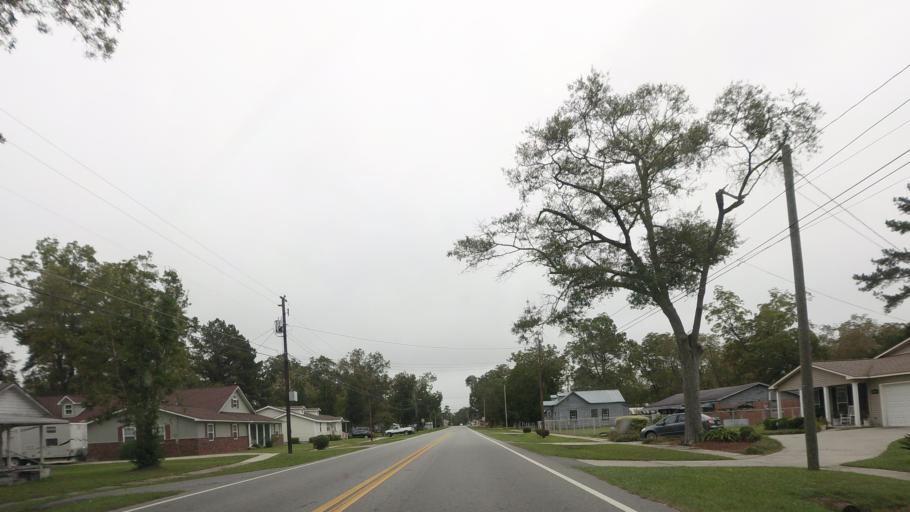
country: US
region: Georgia
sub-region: Berrien County
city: Enigma
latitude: 31.3782
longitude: -83.2250
